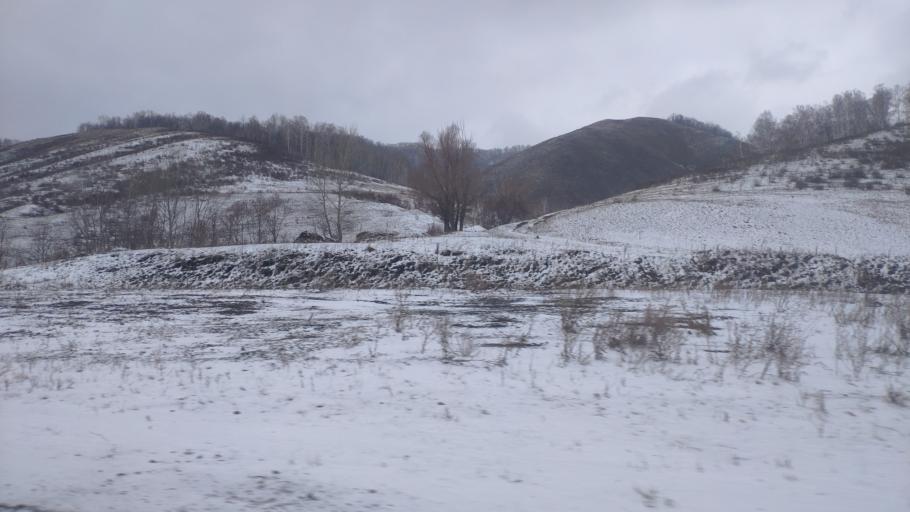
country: RU
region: Bashkortostan
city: Isyangulovo
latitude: 52.1619
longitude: 56.9066
